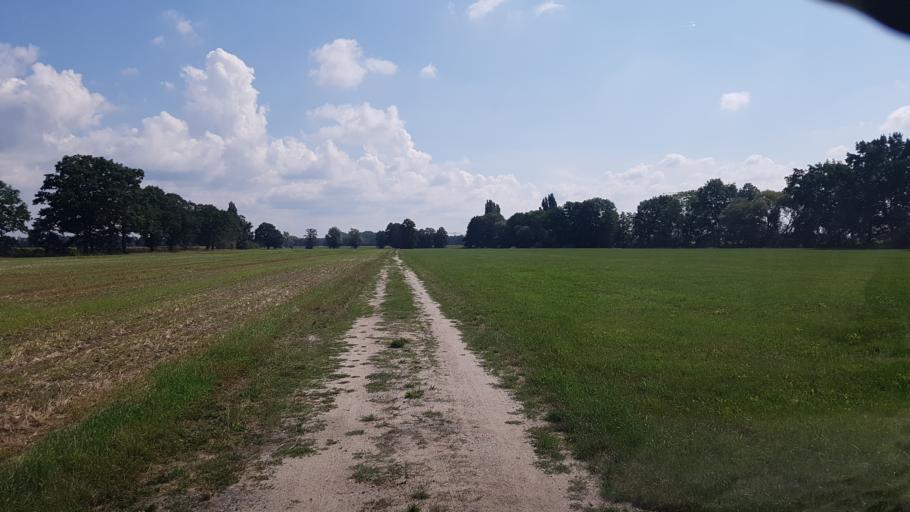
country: DE
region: Brandenburg
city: Sonnewalde
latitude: 51.6719
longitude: 13.6517
